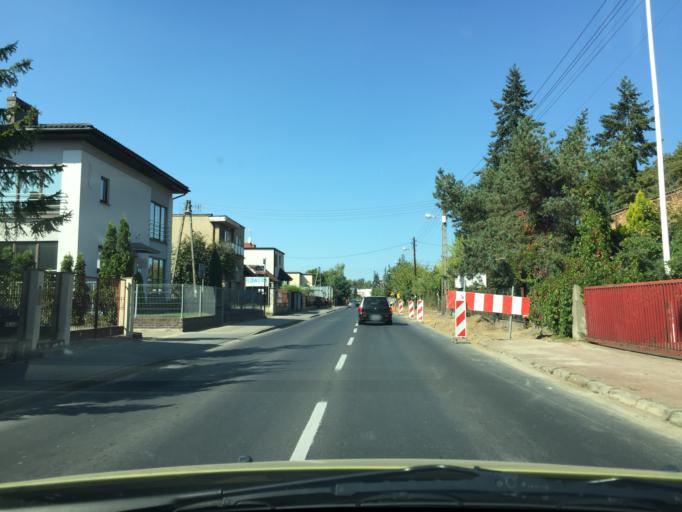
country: PL
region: Greater Poland Voivodeship
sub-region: Powiat poznanski
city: Plewiska
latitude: 52.3837
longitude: 16.8304
